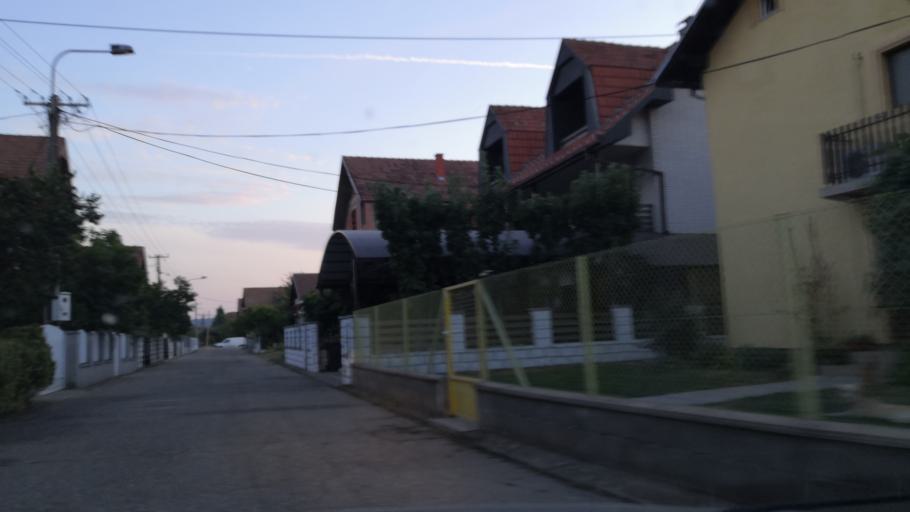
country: RS
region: Central Serbia
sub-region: Borski Okrug
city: Negotin
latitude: 44.2420
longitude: 22.5289
